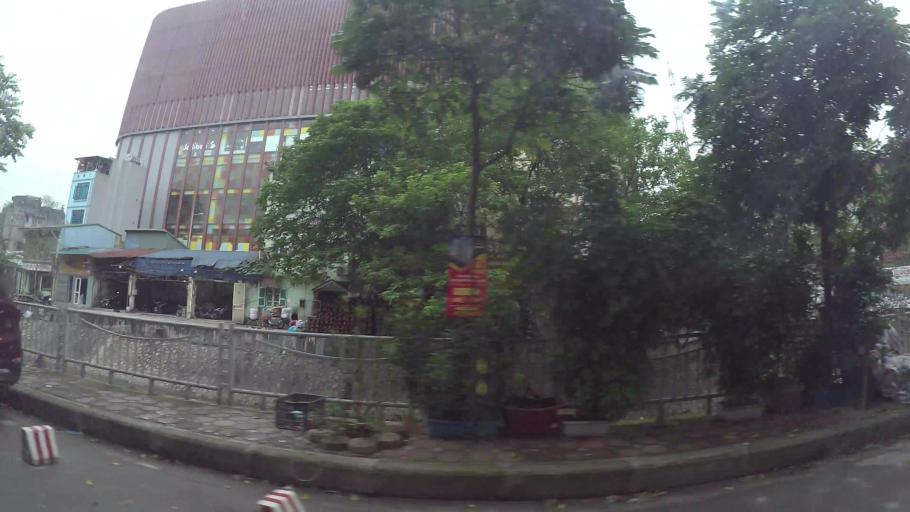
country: VN
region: Ha Noi
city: Dong Da
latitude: 21.0066
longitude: 105.8324
